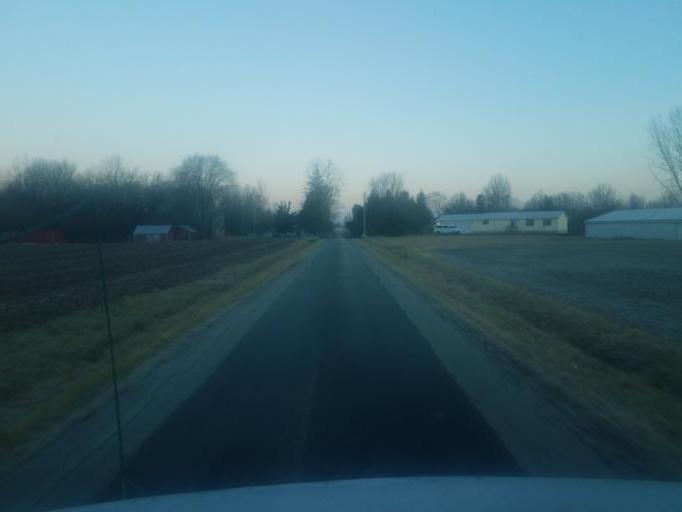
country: US
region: Ohio
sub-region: Crawford County
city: Galion
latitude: 40.7529
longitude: -82.8677
